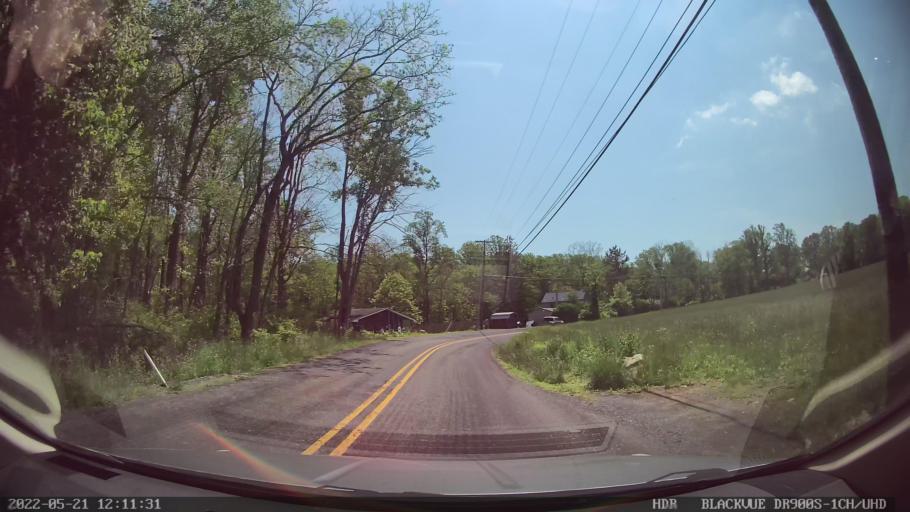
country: US
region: Pennsylvania
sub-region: Berks County
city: Topton
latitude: 40.4534
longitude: -75.6780
